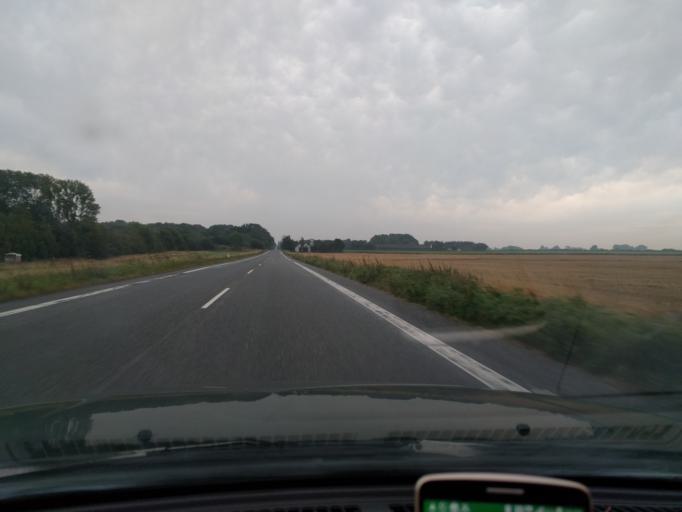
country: DK
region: Zealand
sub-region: Guldborgsund Kommune
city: Norre Alslev
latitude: 54.9306
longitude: 11.8714
